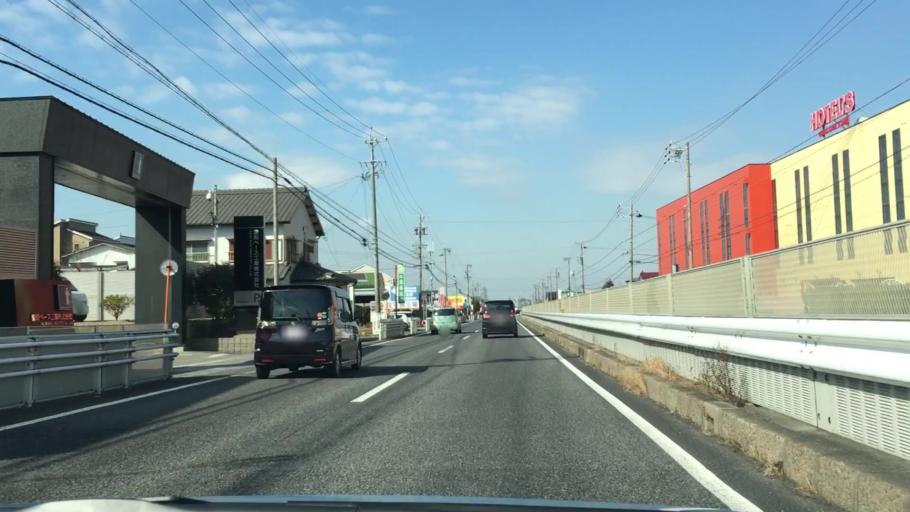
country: JP
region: Aichi
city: Okazaki
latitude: 34.9193
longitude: 137.2077
